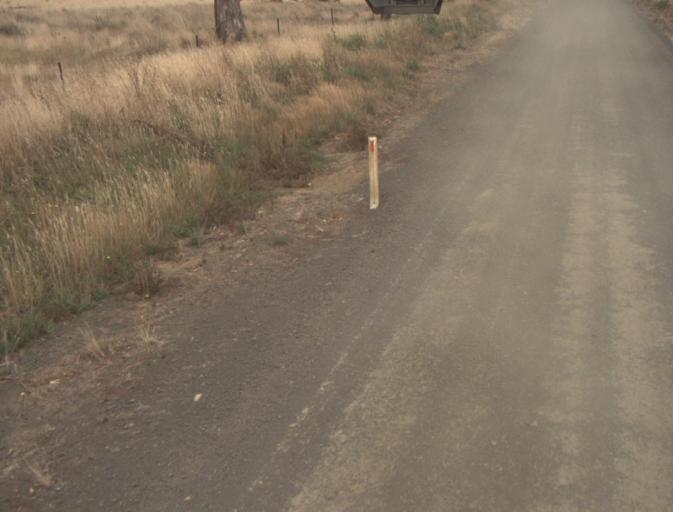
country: AU
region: Tasmania
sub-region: Northern Midlands
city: Evandale
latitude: -41.5260
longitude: 147.3618
